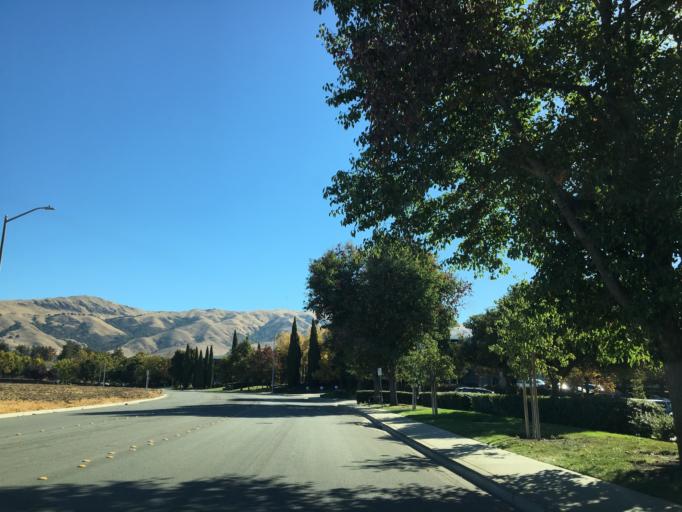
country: US
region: California
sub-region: Santa Clara County
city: Milpitas
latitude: 37.4976
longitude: -121.9319
